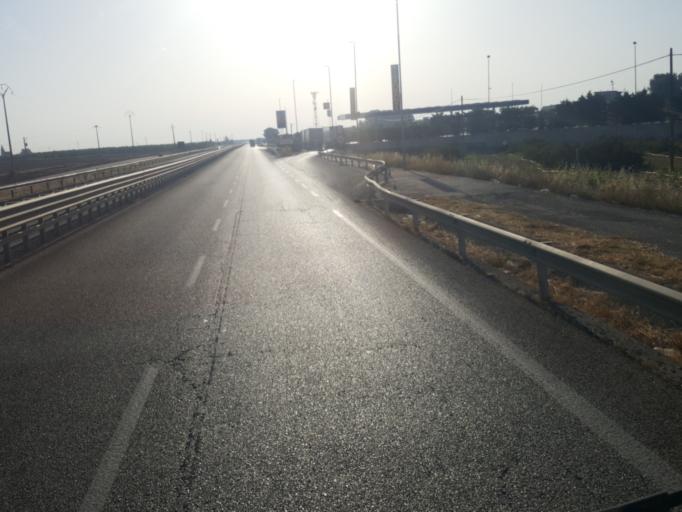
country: IT
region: Apulia
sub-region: Provincia di Foggia
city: Cerignola
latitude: 41.2663
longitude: 15.9399
